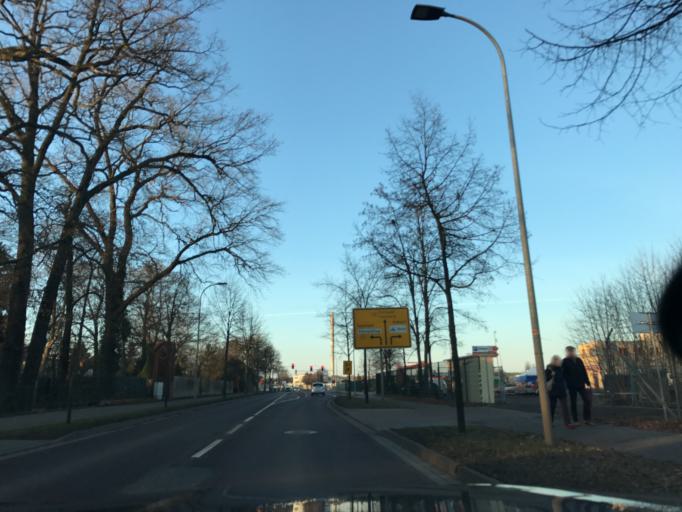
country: DE
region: Saxony-Anhalt
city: Genthin
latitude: 52.4138
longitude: 12.1506
